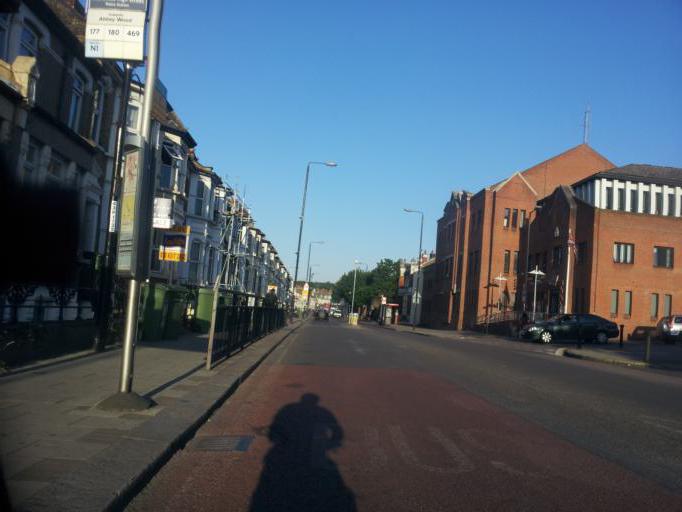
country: GB
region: England
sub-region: Greater London
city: Abbey Wood
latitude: 51.4869
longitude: 0.0950
